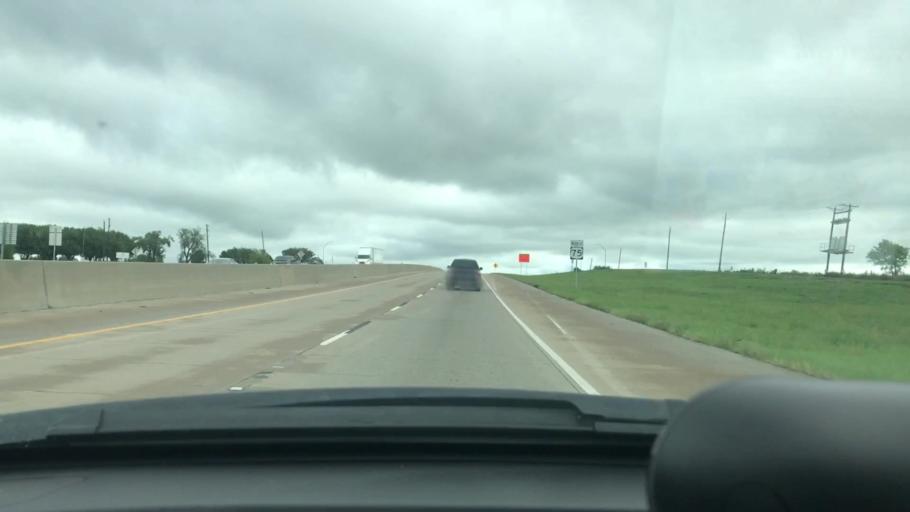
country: US
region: Texas
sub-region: Grayson County
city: Howe
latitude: 33.5306
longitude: -96.6116
